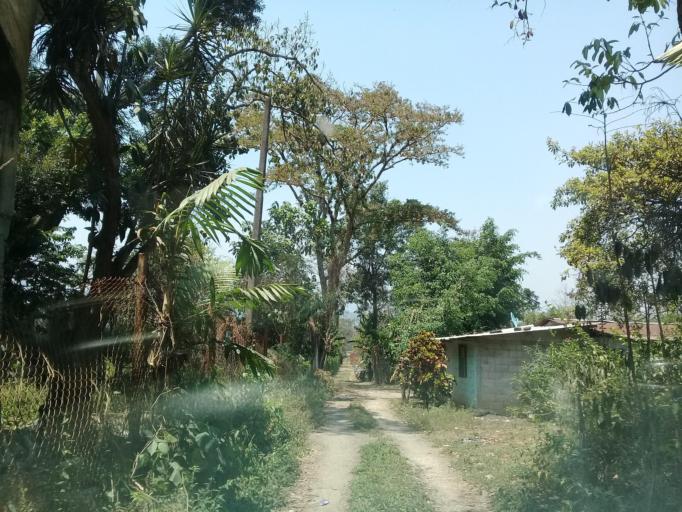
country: MX
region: Veracruz
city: Paraje Nuevo
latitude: 18.8735
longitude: -96.8752
